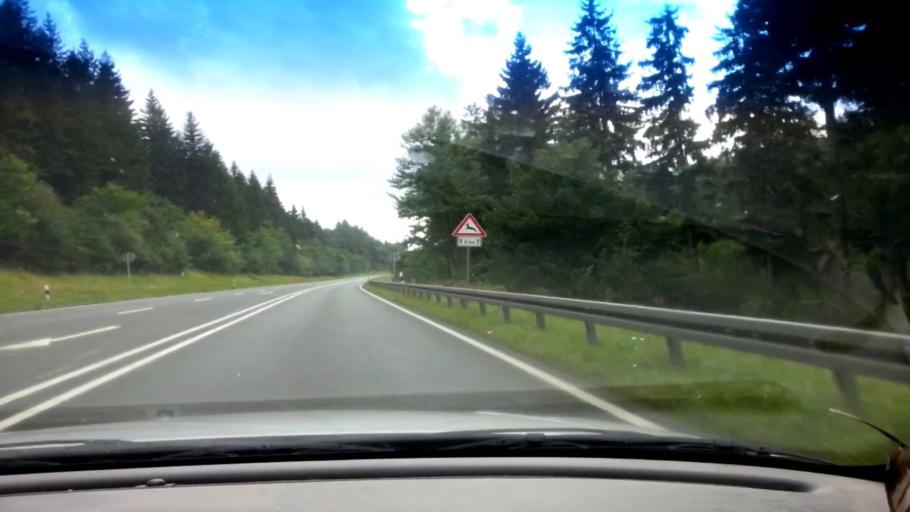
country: DE
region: Bavaria
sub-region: Upper Franconia
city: Bischofsgrun
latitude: 50.0530
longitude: 11.7746
